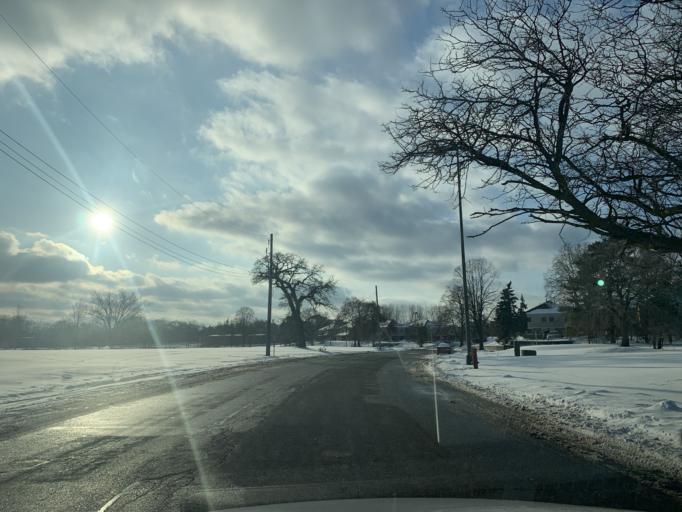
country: US
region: Minnesota
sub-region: Hennepin County
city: Minneapolis
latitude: 44.9830
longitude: -93.2950
